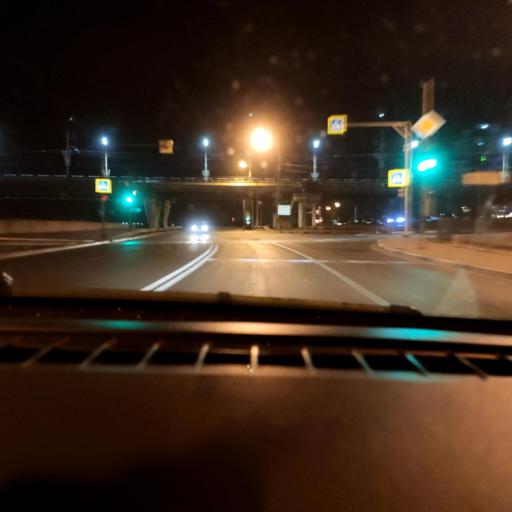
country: RU
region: Voronezj
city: Voronezh
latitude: 51.6691
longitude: 39.2224
